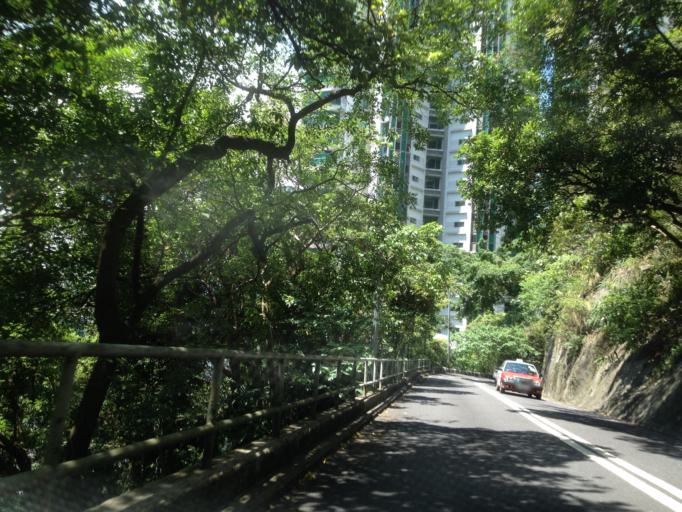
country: HK
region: Central and Western
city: Central
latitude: 22.2735
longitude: 114.1586
